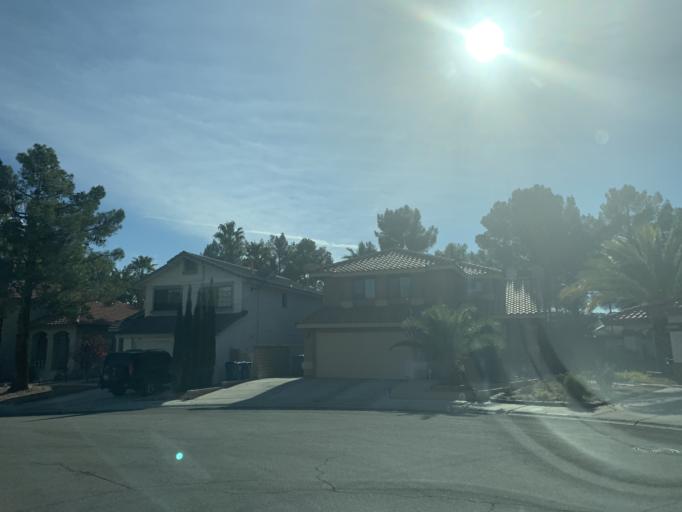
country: US
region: Nevada
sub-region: Clark County
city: Summerlin South
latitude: 36.1340
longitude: -115.2954
